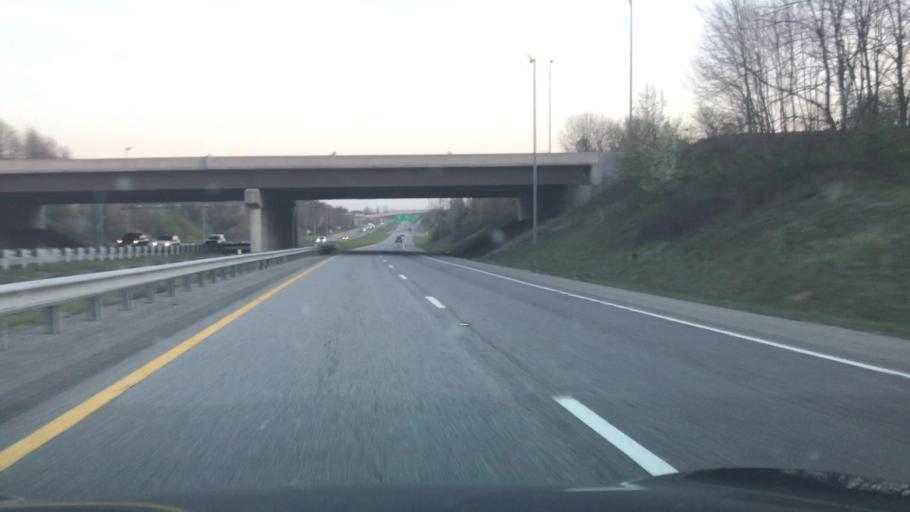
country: US
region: Virginia
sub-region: Montgomery County
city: Merrimac
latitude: 37.1656
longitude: -80.4151
